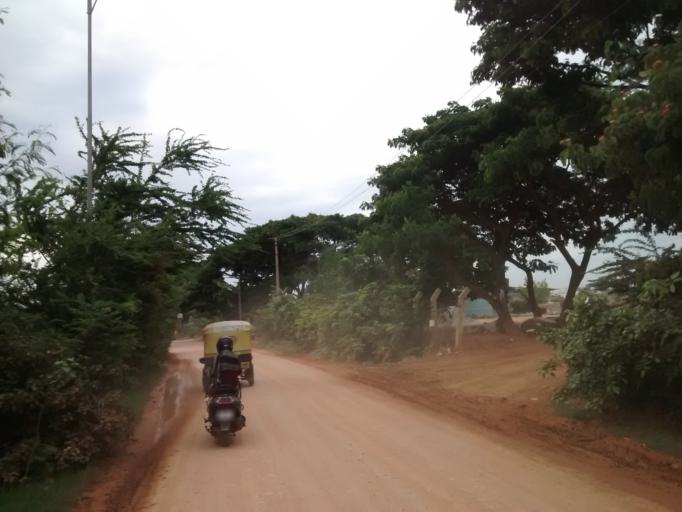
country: IN
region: Karnataka
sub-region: Bangalore Urban
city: Bangalore
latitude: 12.9410
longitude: 77.6789
